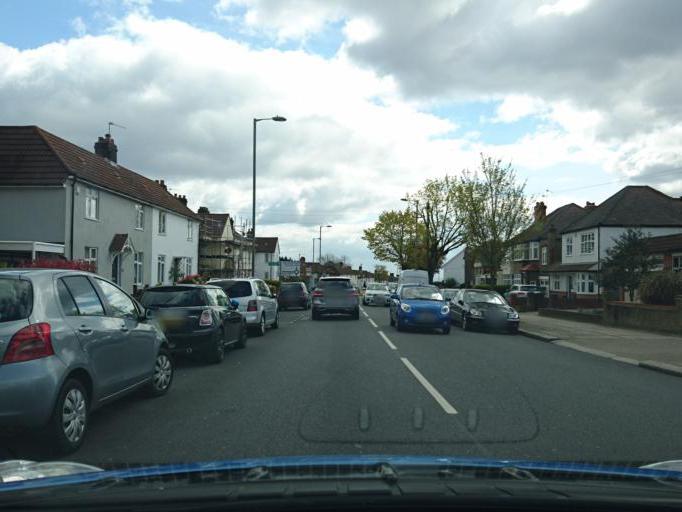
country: GB
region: England
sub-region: Greater London
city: Hadley Wood
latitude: 51.6283
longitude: -0.1631
